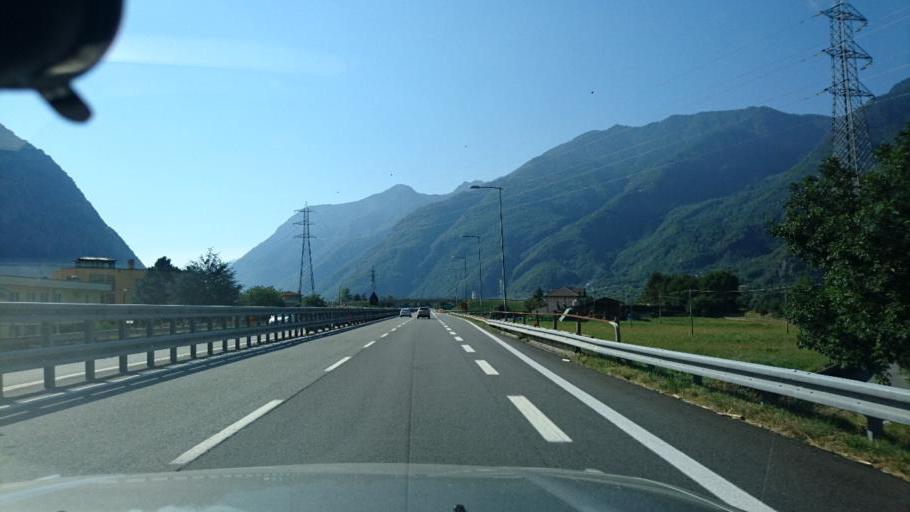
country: IT
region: Aosta Valley
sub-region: Valle d'Aosta
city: Verres
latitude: 45.6723
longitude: 7.6822
